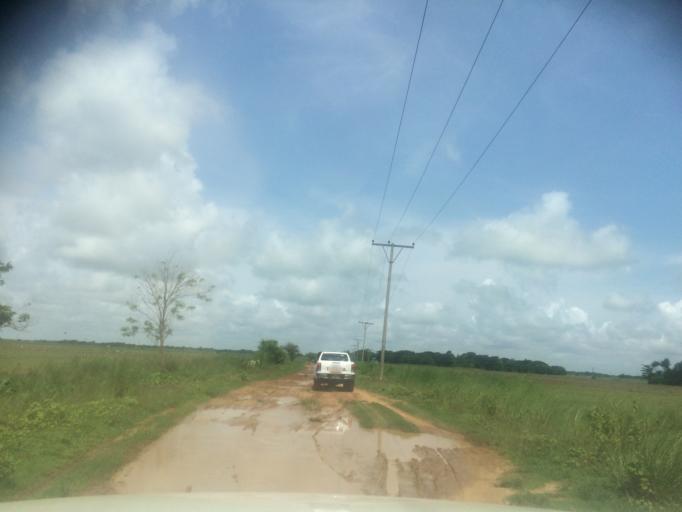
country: MM
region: Bago
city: Tharyarwady
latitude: 17.3176
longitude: 95.9032
